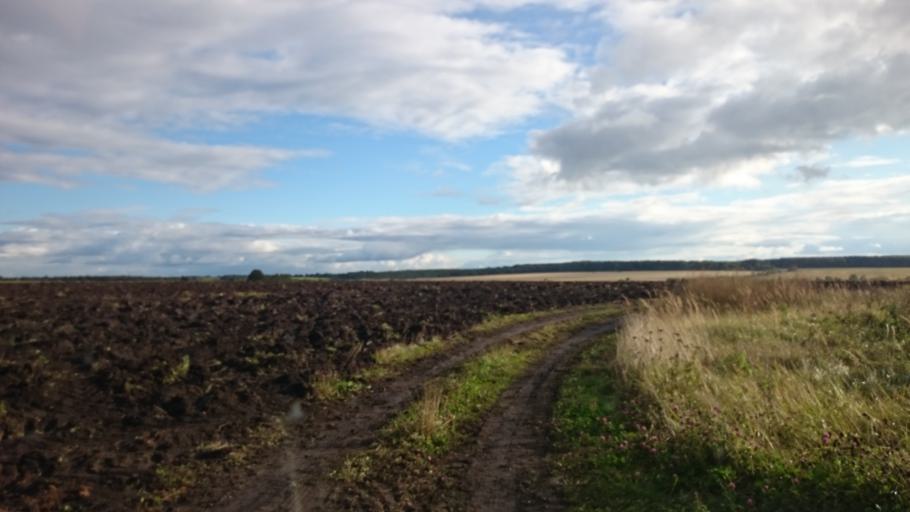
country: RU
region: Mordoviya
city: Kadoshkino
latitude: 54.0269
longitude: 44.5161
